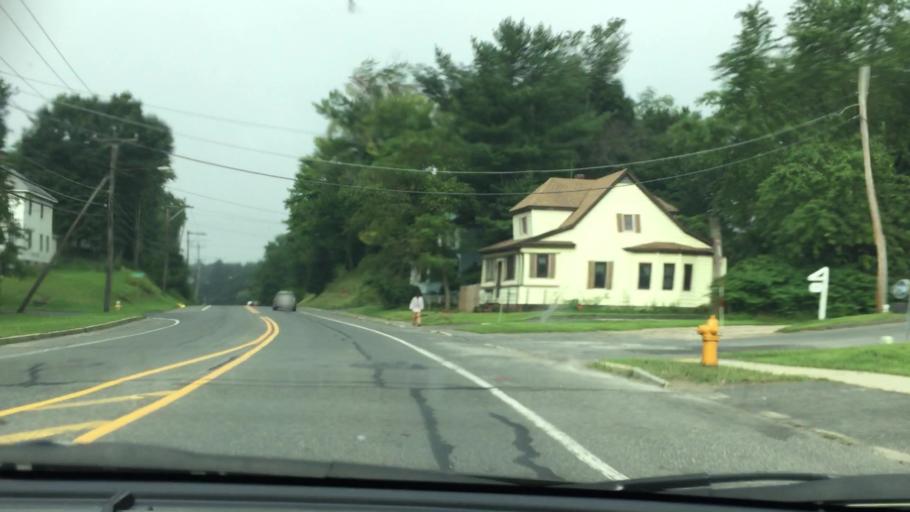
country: US
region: Massachusetts
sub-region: Berkshire County
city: Pittsfield
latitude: 42.4438
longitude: -73.2712
